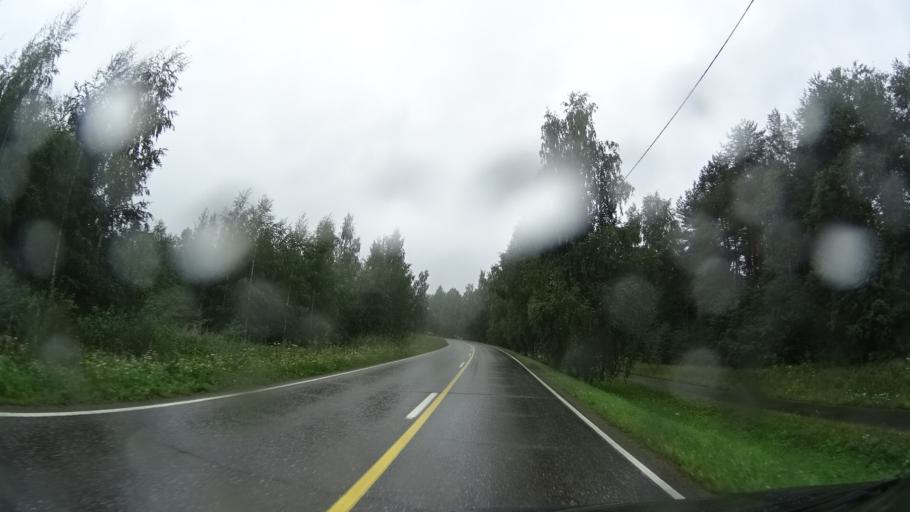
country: FI
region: North Karelia
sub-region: Keski-Karjala
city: Raeaekkylae
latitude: 62.3132
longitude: 29.5955
